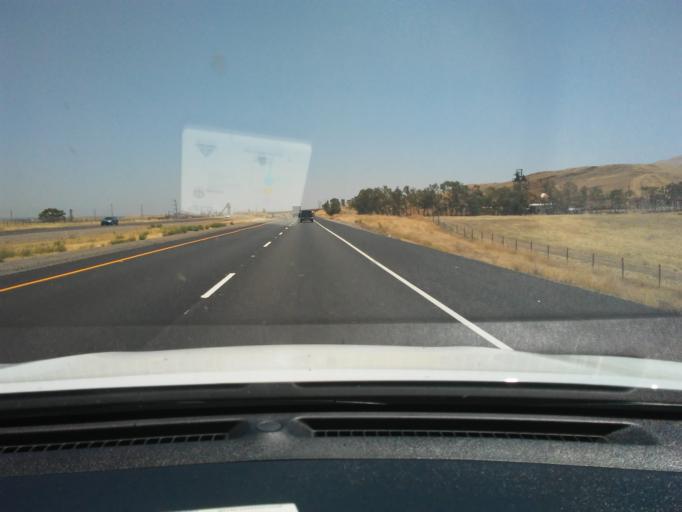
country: US
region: California
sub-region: San Joaquin County
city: Tracy
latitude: 37.6183
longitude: -121.3694
